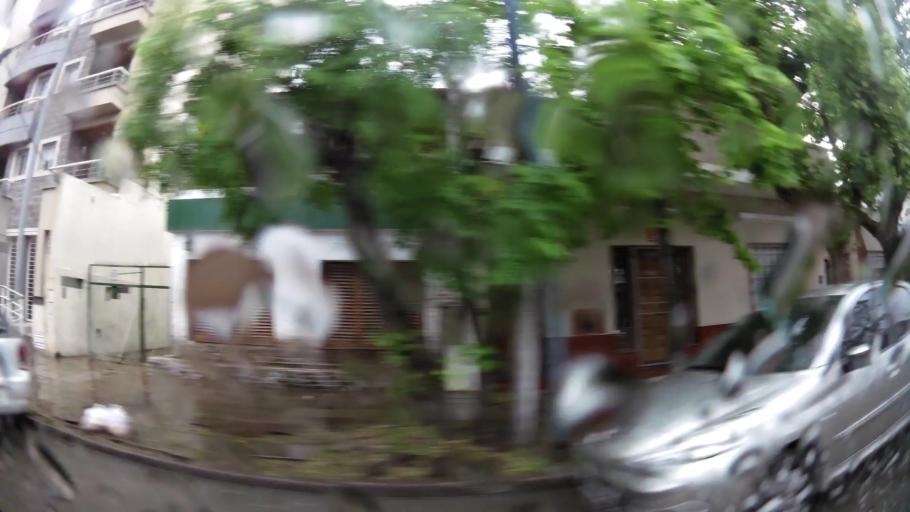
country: AR
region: Buenos Aires
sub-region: Partido de Lanus
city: Lanus
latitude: -34.7164
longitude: -58.3957
